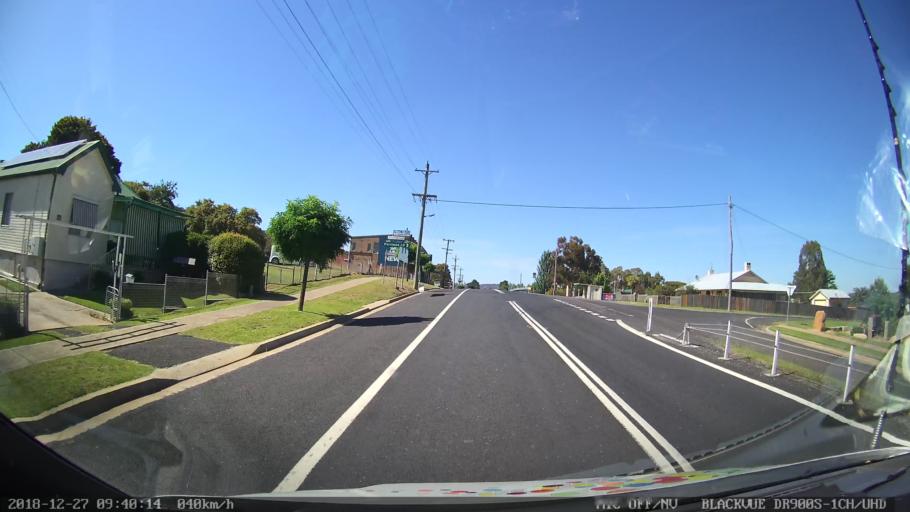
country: AU
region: New South Wales
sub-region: Lithgow
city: Portland
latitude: -33.2990
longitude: 150.0331
